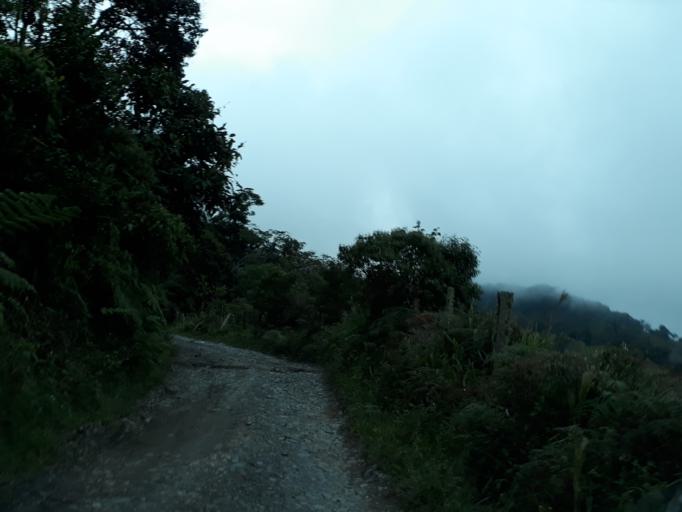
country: CO
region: Boyaca
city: Muzo
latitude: 5.3816
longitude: -74.0769
